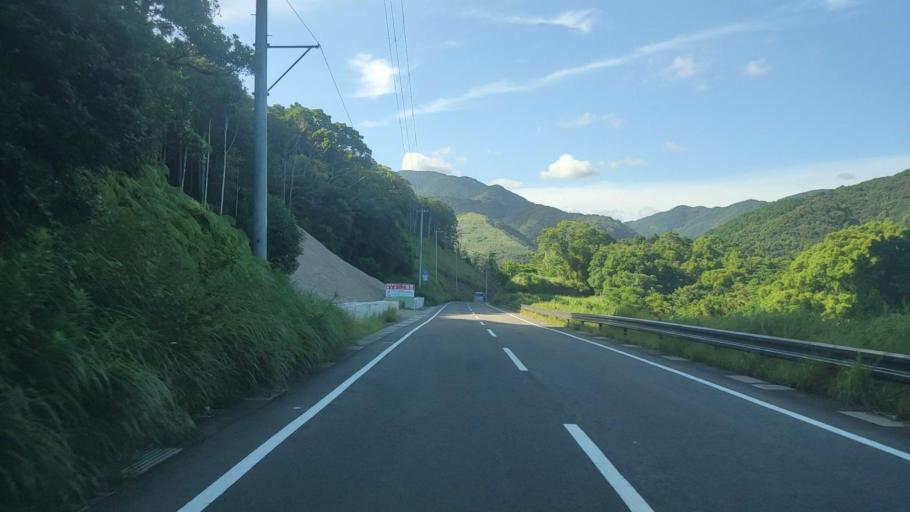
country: JP
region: Wakayama
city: Tanabe
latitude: 33.5114
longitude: 135.6020
